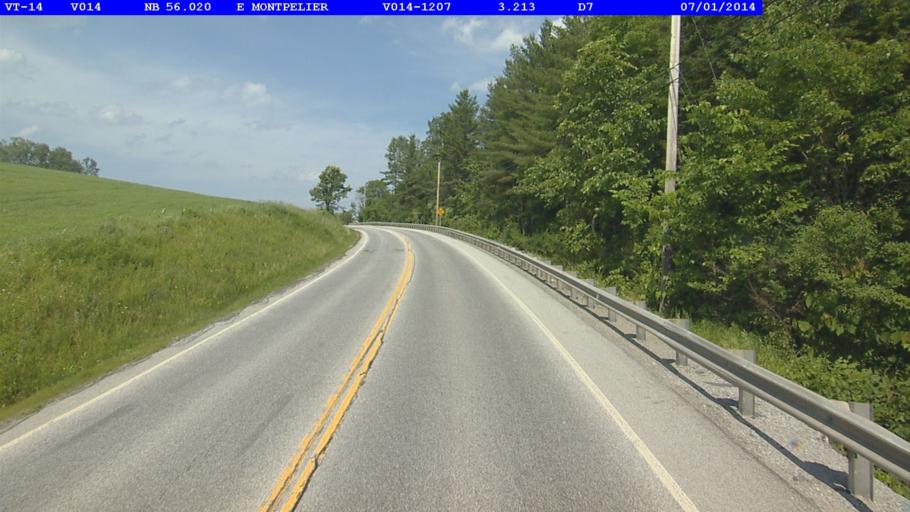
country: US
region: Vermont
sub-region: Washington County
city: Barre
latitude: 44.2784
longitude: -72.4755
